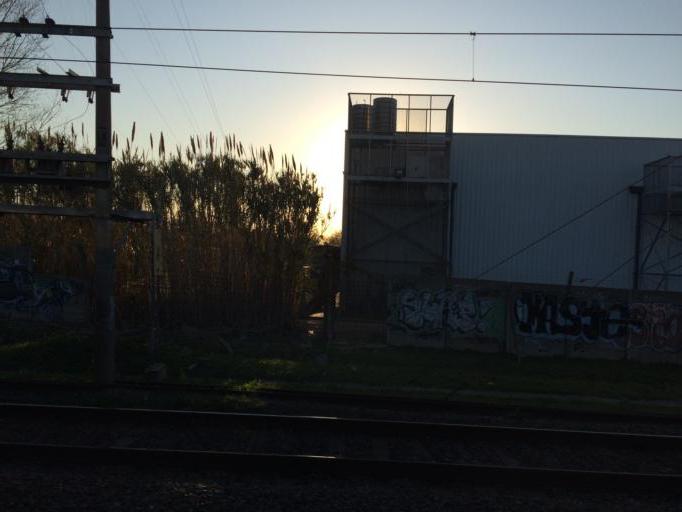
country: AR
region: Buenos Aires
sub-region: Partido de Lanus
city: Lanus
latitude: -34.7218
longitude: -58.3930
